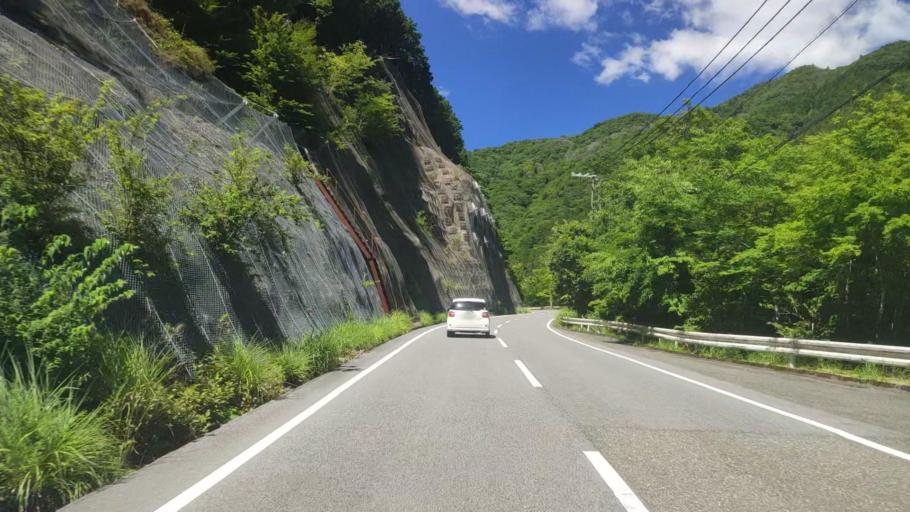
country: JP
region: Mie
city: Owase
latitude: 34.1947
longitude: 135.9980
